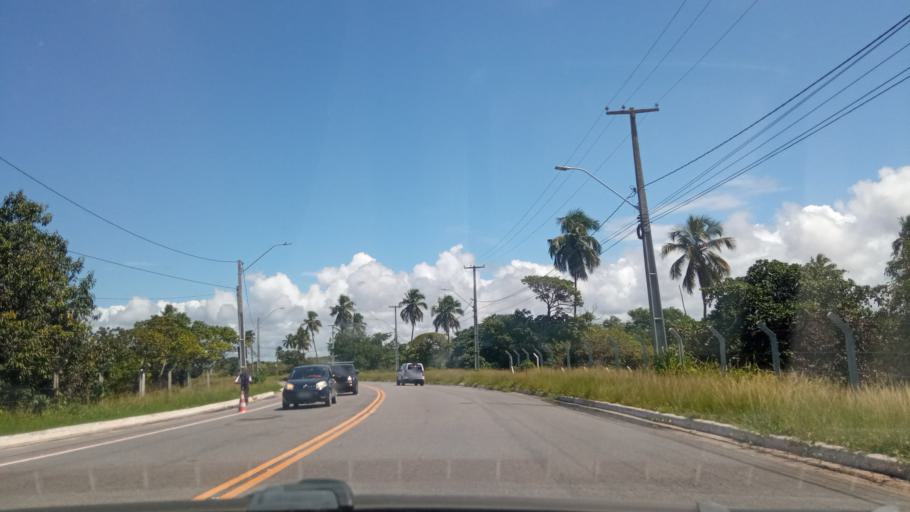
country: BR
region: Pernambuco
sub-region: Jaboatao Dos Guararapes
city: Jaboatao
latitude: -8.2297
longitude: -34.9345
